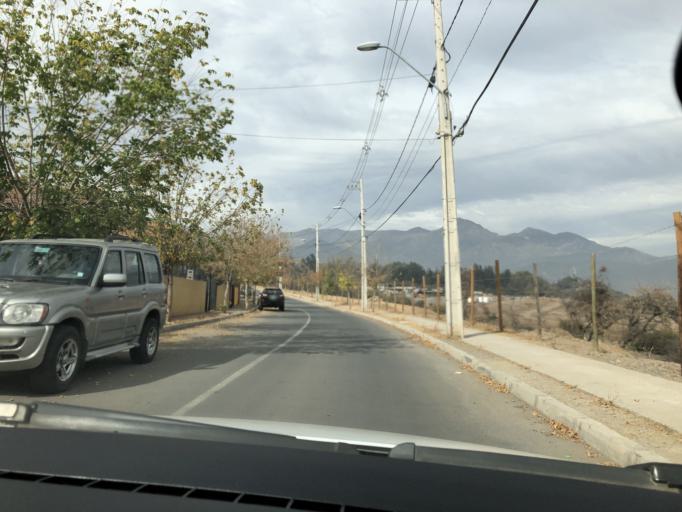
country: CL
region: Santiago Metropolitan
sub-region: Provincia de Cordillera
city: Puente Alto
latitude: -33.5888
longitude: -70.5343
